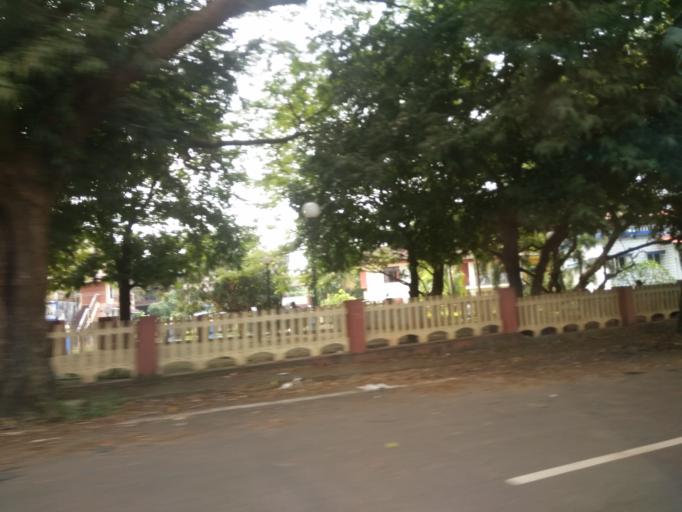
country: IN
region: Goa
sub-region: North Goa
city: Panaji
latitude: 15.5184
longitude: 73.8291
